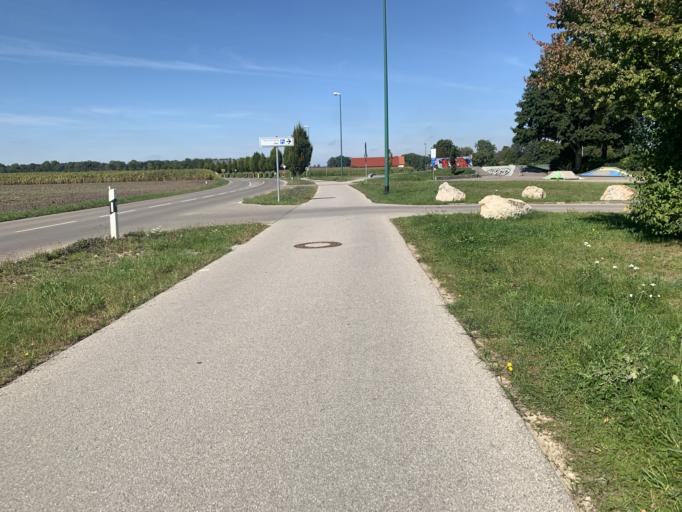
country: DE
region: Bavaria
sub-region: Swabia
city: Kissing
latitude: 48.3063
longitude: 10.9805
